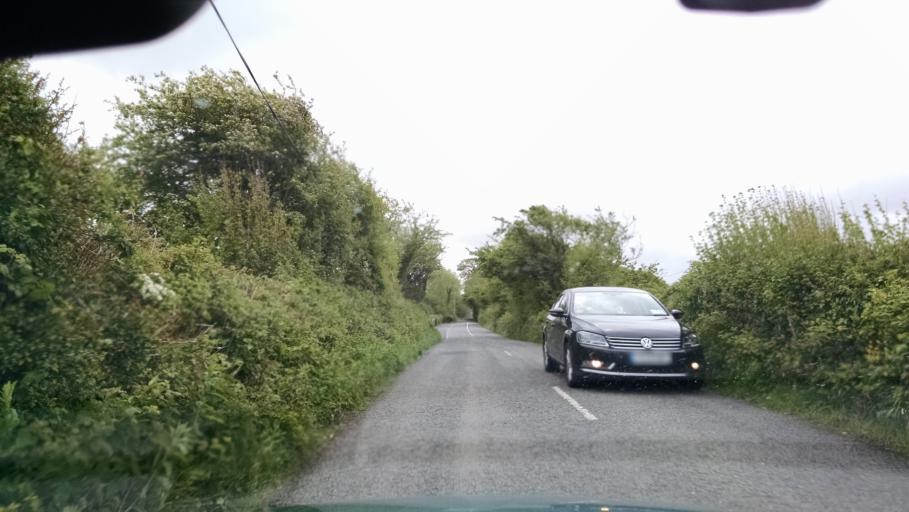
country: IE
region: Connaught
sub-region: County Galway
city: Bearna
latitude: 53.0920
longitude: -9.1585
